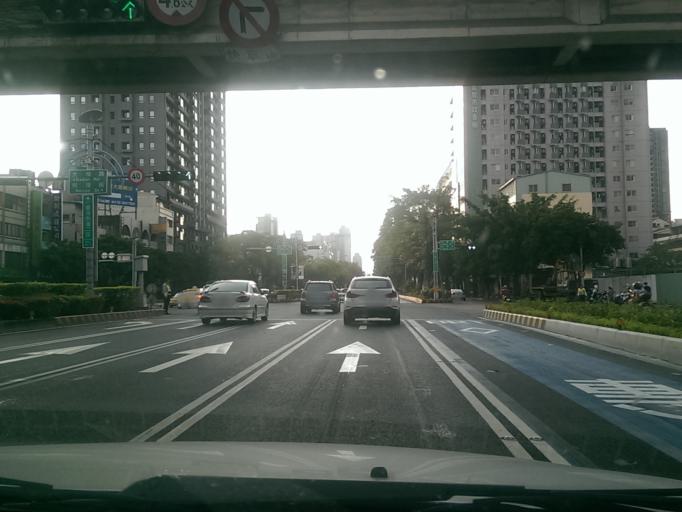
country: TW
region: Taiwan
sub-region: Taichung City
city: Taichung
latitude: 24.1606
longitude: 120.6536
